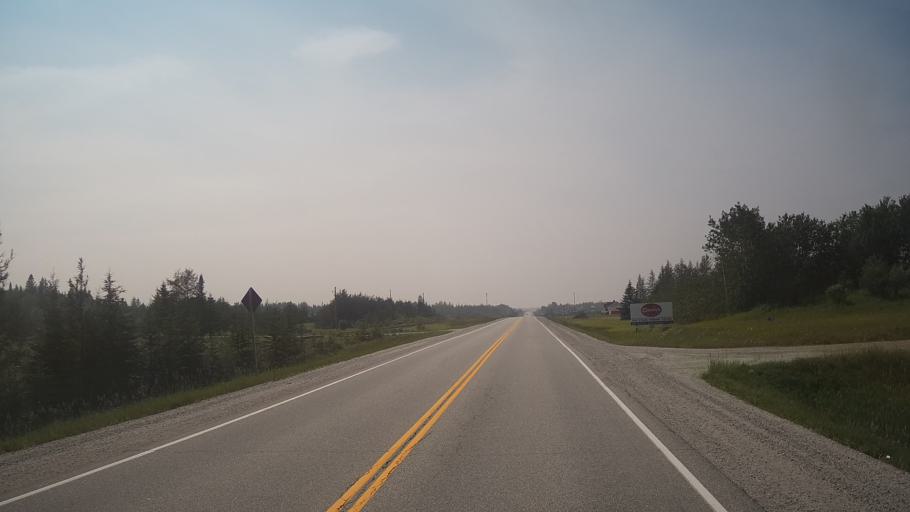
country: CA
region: Ontario
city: Kapuskasing
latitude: 49.3019
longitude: -81.9883
